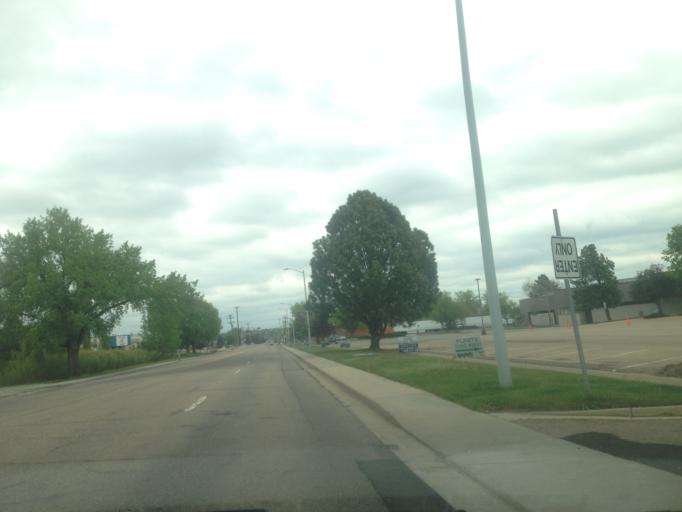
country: US
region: Colorado
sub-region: Boulder County
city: Longmont
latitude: 40.1454
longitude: -105.1215
